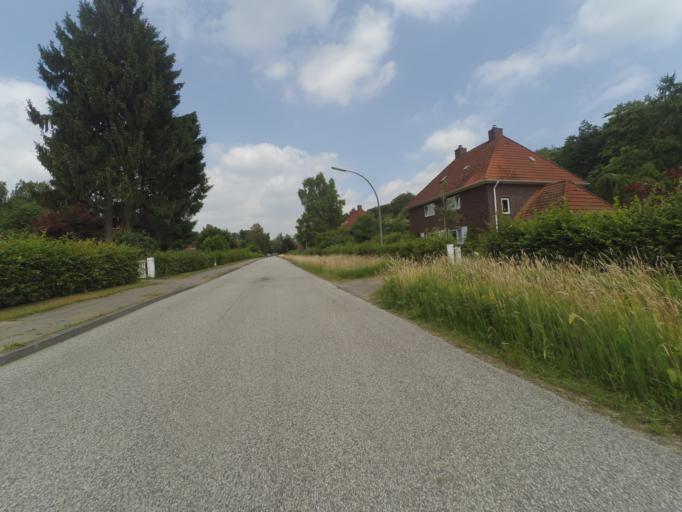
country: DE
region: Hamburg
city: Farmsen-Berne
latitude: 53.6311
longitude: 10.1251
